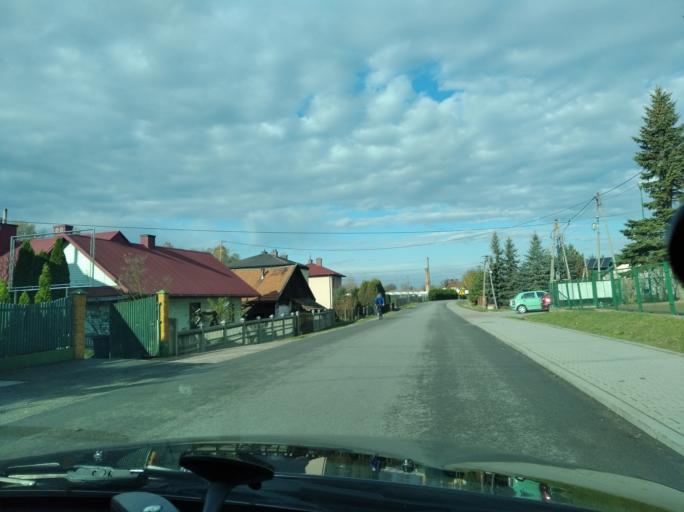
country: PL
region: Subcarpathian Voivodeship
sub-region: Powiat debicki
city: Brzeznica
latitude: 50.0511
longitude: 21.4857
